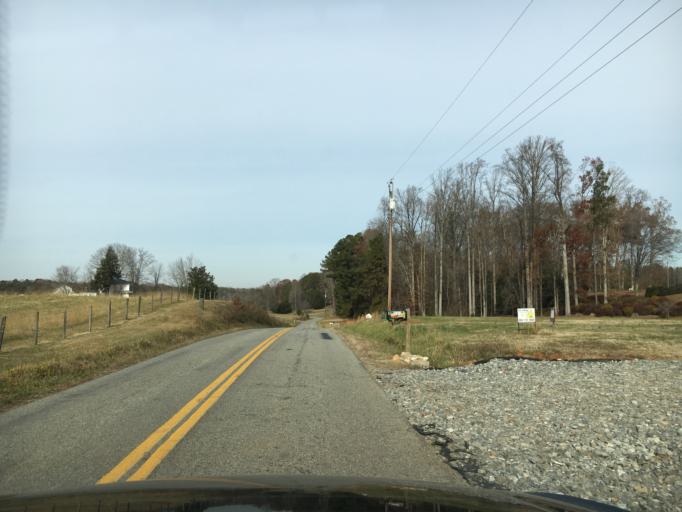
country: US
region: Virginia
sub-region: Henrico County
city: Wyndham
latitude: 37.7347
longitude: -77.7011
